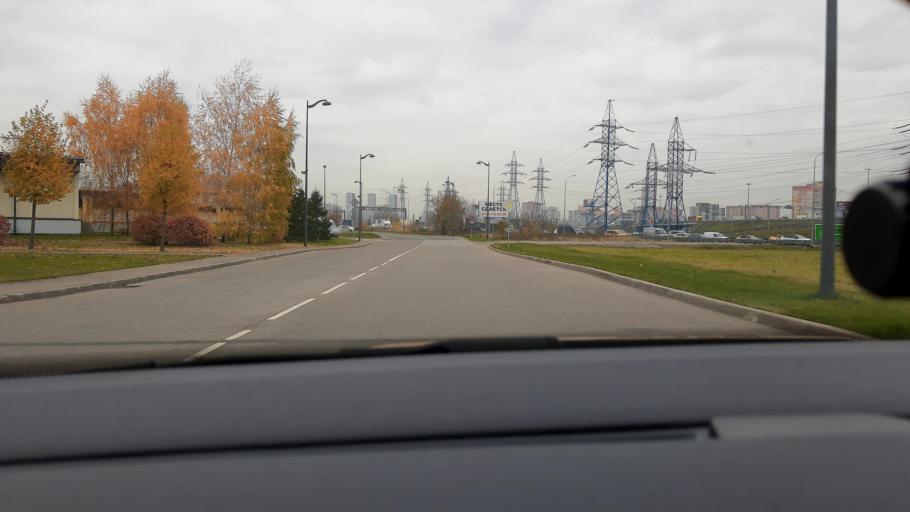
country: RU
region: Moskovskaya
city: Lyubertsy
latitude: 55.6612
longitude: 37.8835
